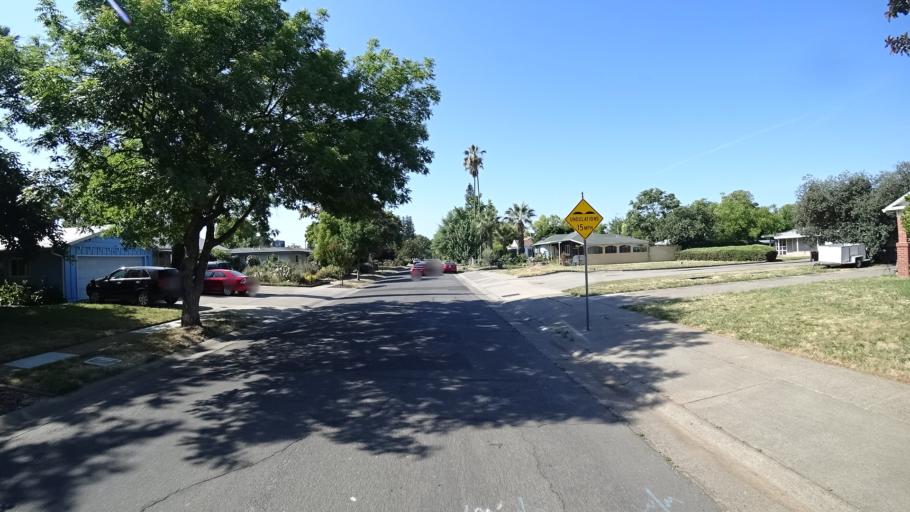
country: US
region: California
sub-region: Sacramento County
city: Florin
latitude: 38.5376
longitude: -121.4311
